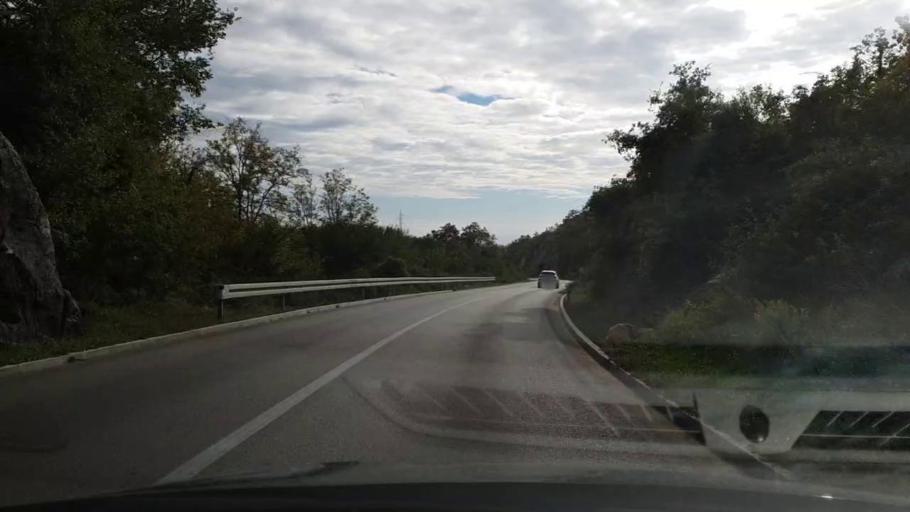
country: ME
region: Herceg Novi
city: Herceg-Novi
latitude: 42.4767
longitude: 18.5293
